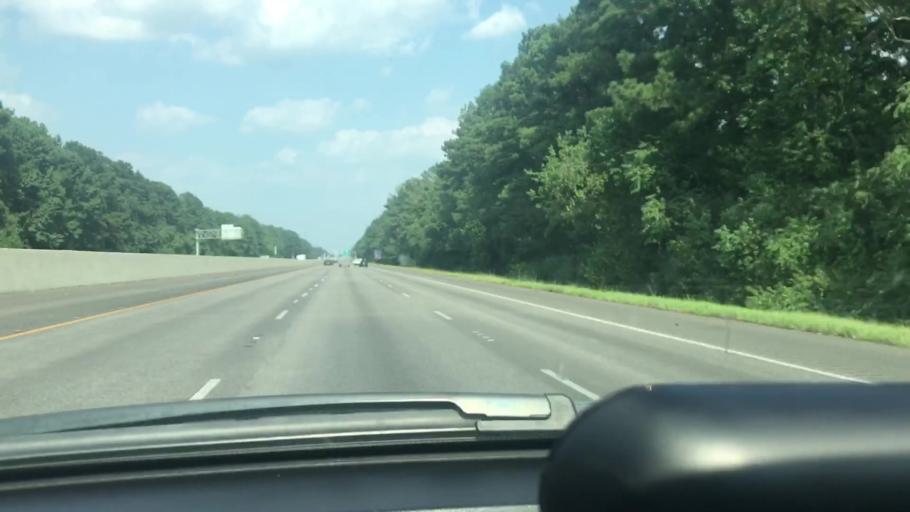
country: US
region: Louisiana
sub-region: Livingston Parish
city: Walker
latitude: 30.4681
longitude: -90.8834
